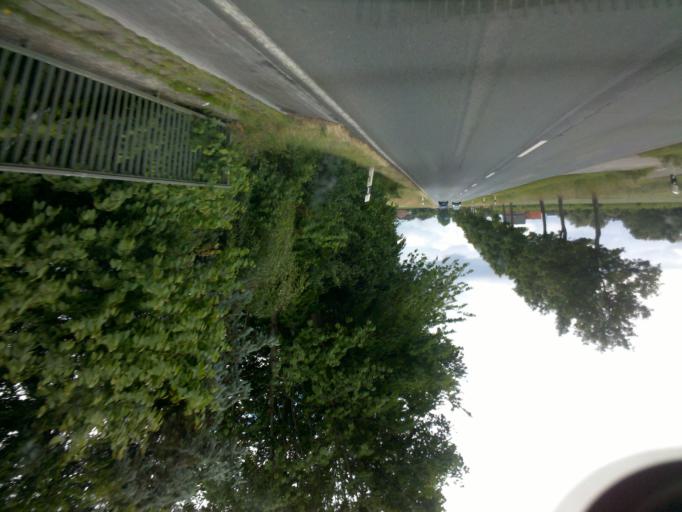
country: DE
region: North Rhine-Westphalia
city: Erwitte
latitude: 51.6298
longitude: 8.3136
